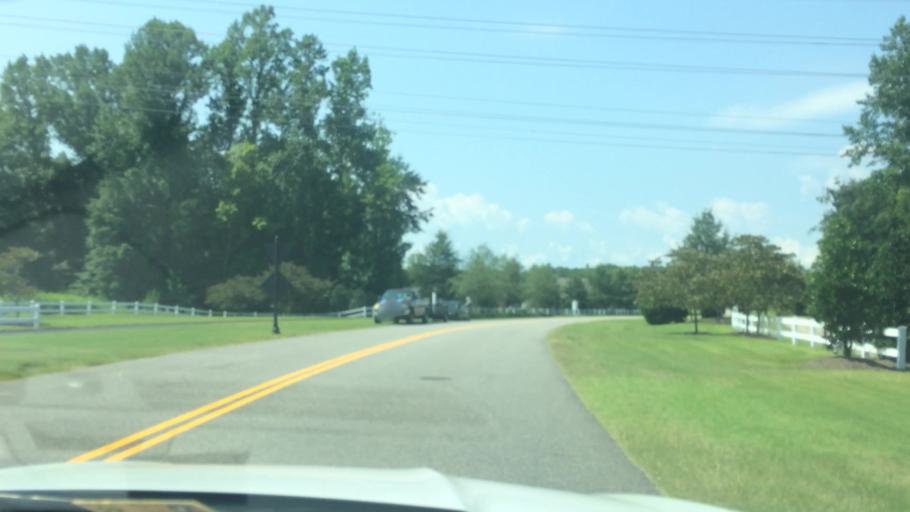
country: US
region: Virginia
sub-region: James City County
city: Williamsburg
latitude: 37.3437
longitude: -76.7744
